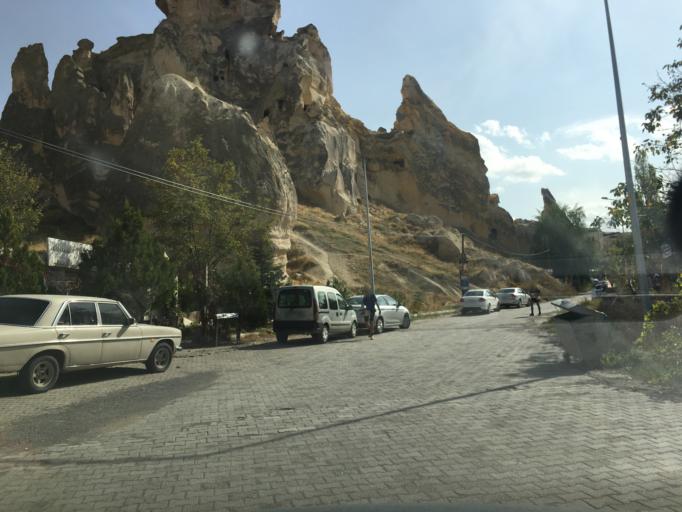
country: TR
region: Nevsehir
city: Goereme
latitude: 38.6685
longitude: 34.8419
